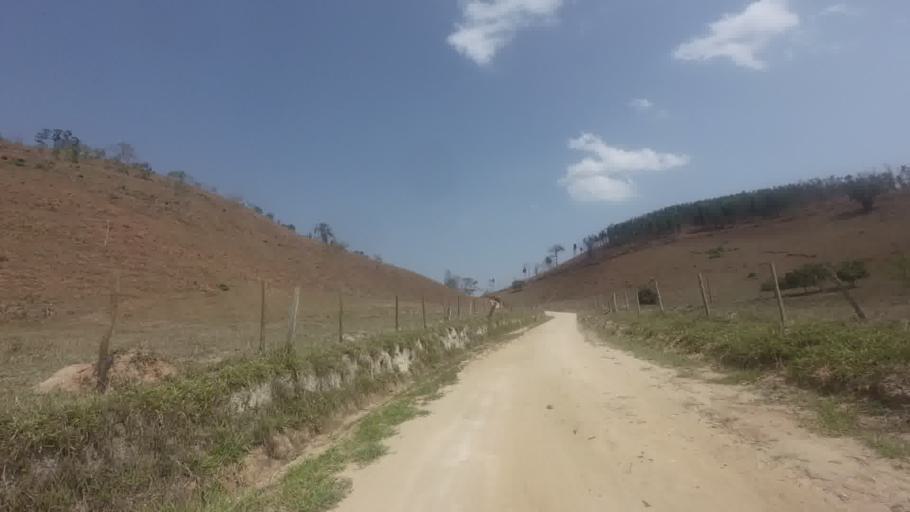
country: BR
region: Espirito Santo
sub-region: Sao Jose Do Calcado
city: Sao Jose do Calcado
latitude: -21.0405
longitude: -41.5271
